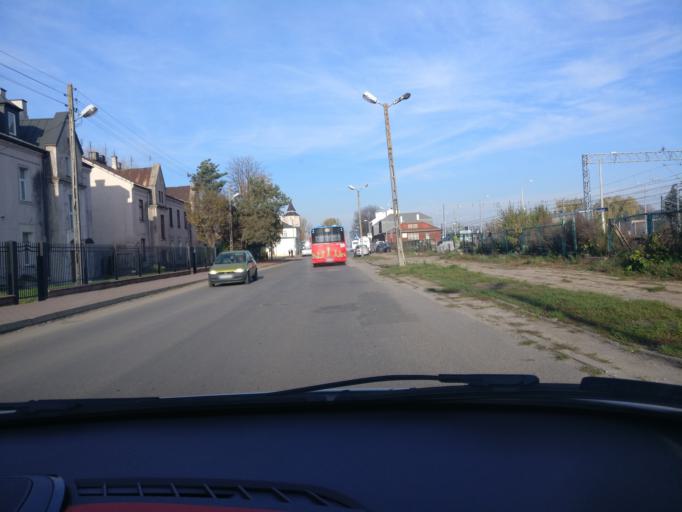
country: PL
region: Lublin Voivodeship
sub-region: Powiat rycki
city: Deblin
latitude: 51.5764
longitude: 21.8362
